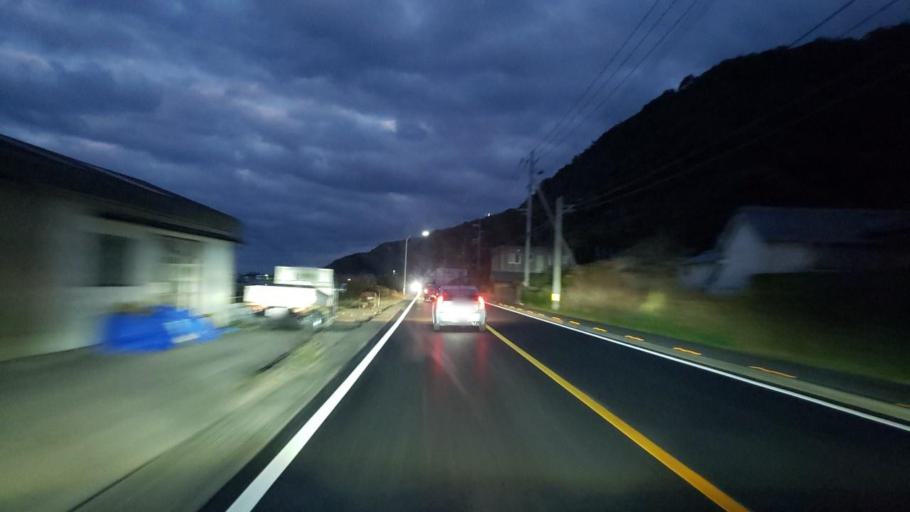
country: JP
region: Tokushima
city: Narutocho-mitsuishi
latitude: 34.2093
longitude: 134.4740
